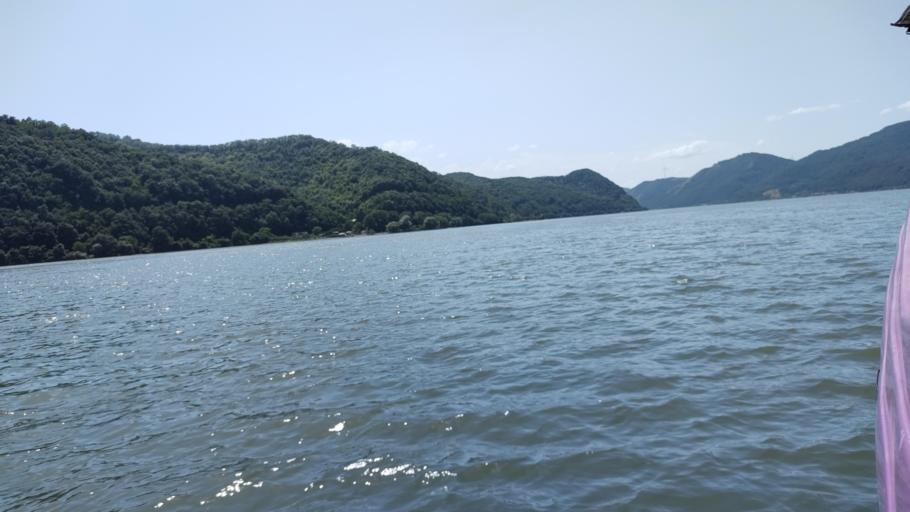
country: RS
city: Radenka
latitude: 44.6573
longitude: 21.8022
